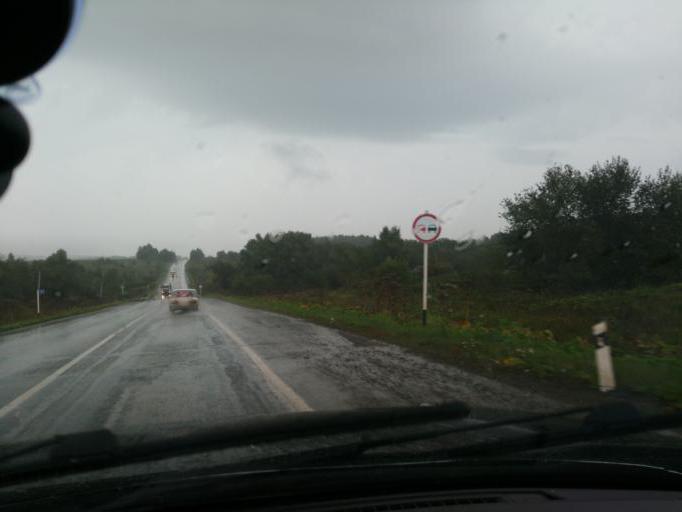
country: RU
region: Perm
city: Osa
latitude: 57.1462
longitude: 55.5291
